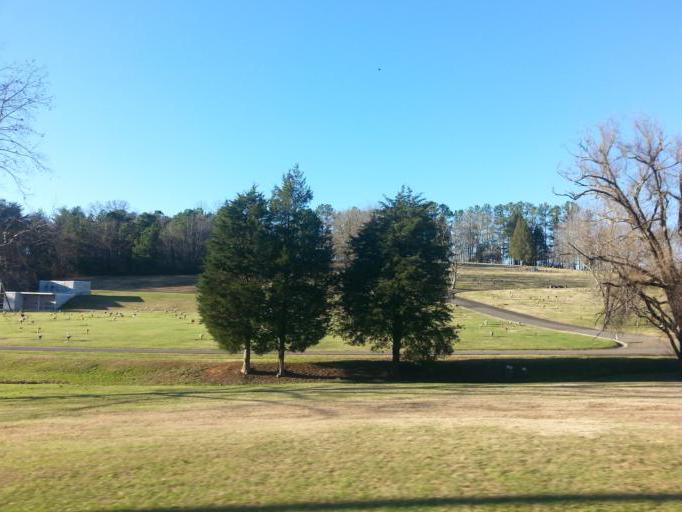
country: US
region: Tennessee
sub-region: Anderson County
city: Oak Ridge
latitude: 36.0642
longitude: -84.2215
